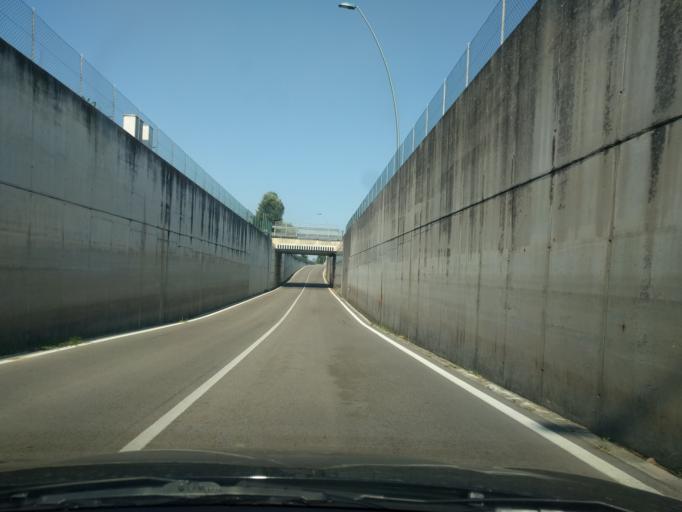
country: IT
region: Veneto
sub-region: Provincia di Rovigo
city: Mardimago
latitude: 45.0926
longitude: 11.8309
